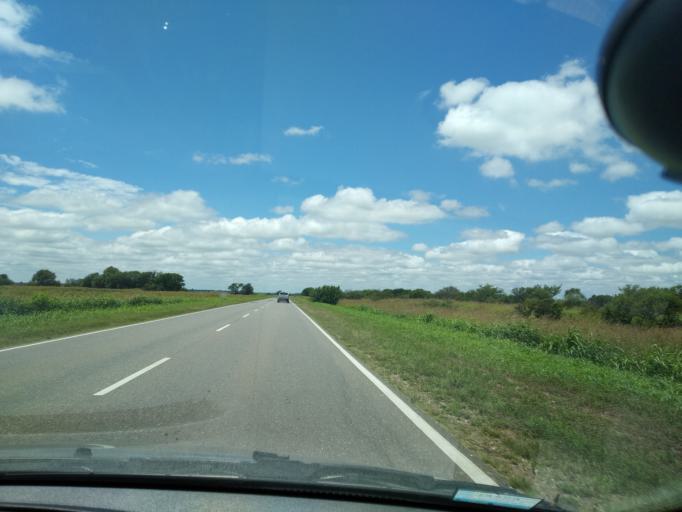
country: AR
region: Cordoba
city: Despenaderos
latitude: -31.6515
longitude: -64.1982
